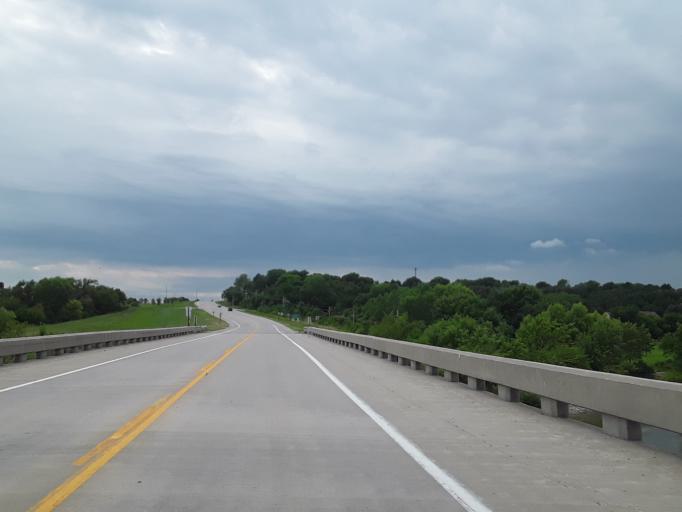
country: US
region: Nebraska
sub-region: Saunders County
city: Yutan
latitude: 41.2343
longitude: -96.3655
